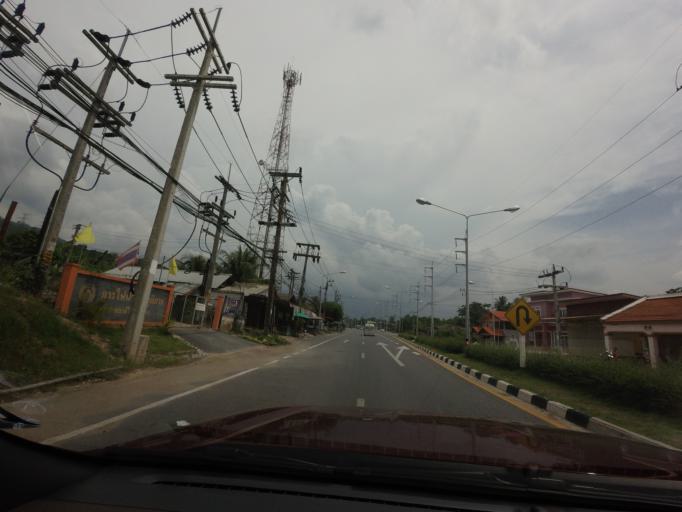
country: TH
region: Yala
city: Yala
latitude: 6.4984
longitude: 101.2668
